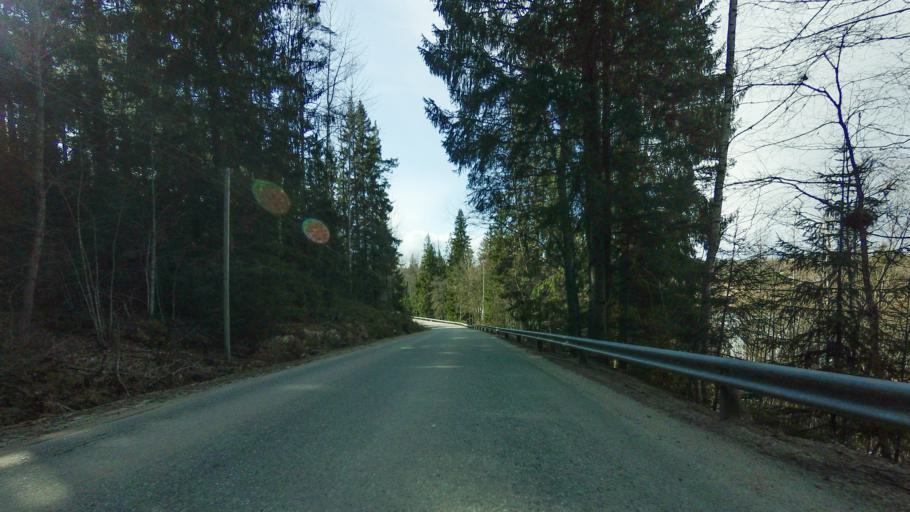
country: FI
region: Varsinais-Suomi
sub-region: Salo
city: Suomusjaervi
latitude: 60.3524
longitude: 23.6563
